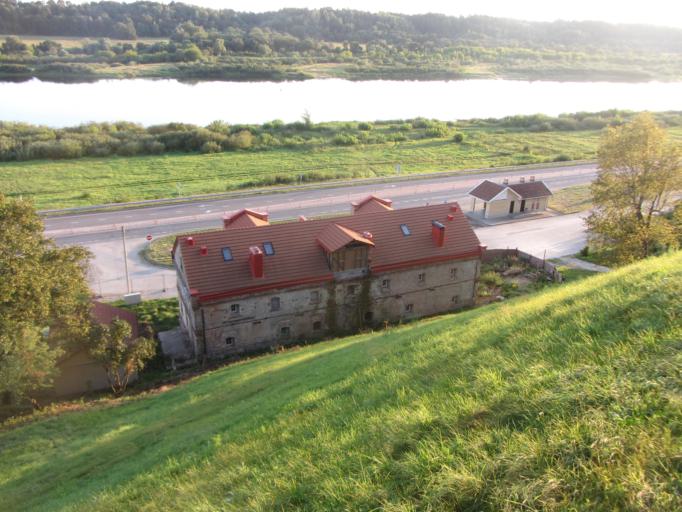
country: LT
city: Ariogala
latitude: 55.0776
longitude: 23.2796
